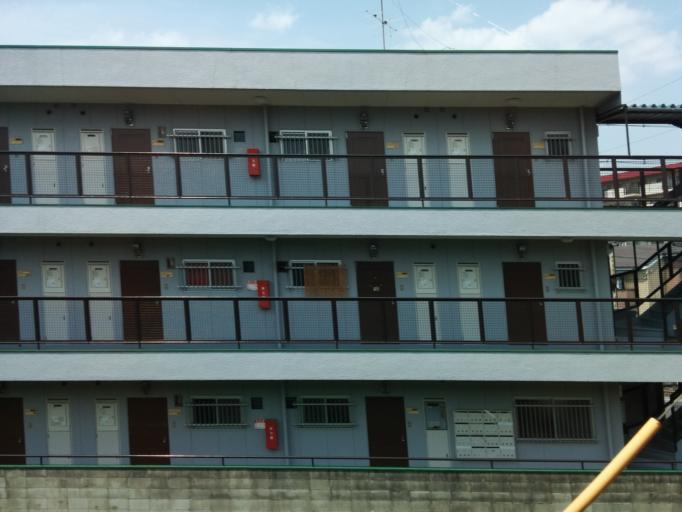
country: JP
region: Osaka
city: Ibaraki
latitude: 34.8080
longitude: 135.5691
